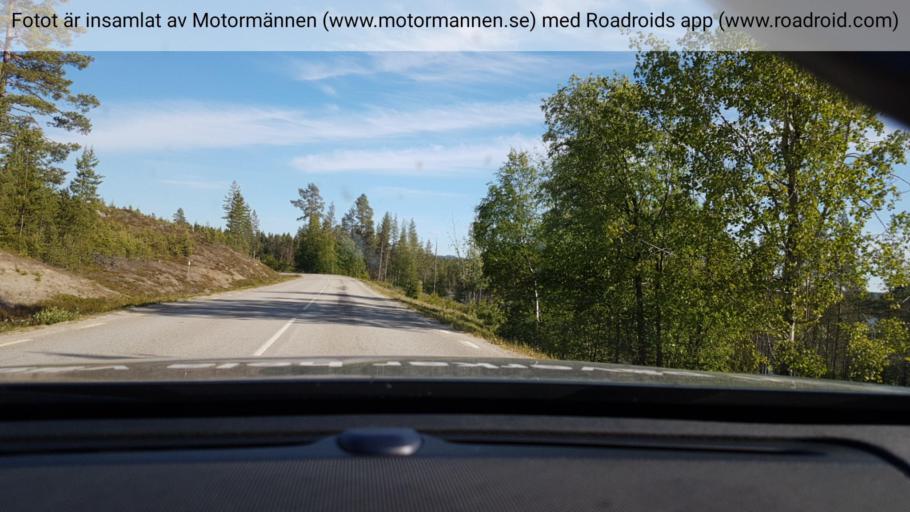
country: SE
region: Vaesterbotten
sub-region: Norsjo Kommun
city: Norsjoe
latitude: 64.7480
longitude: 19.0982
